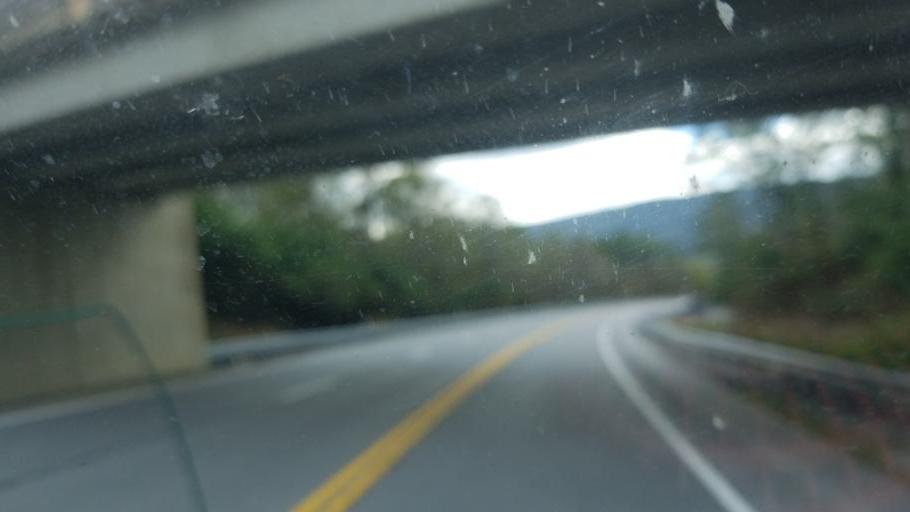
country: US
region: Pennsylvania
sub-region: Fulton County
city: McConnellsburg
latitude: 39.9441
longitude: -78.0093
